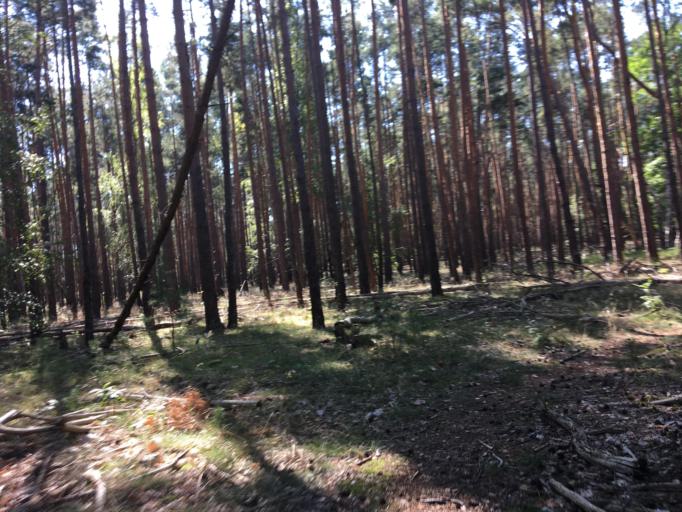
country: DE
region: Brandenburg
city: Gross Koris
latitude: 52.2017
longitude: 13.7408
